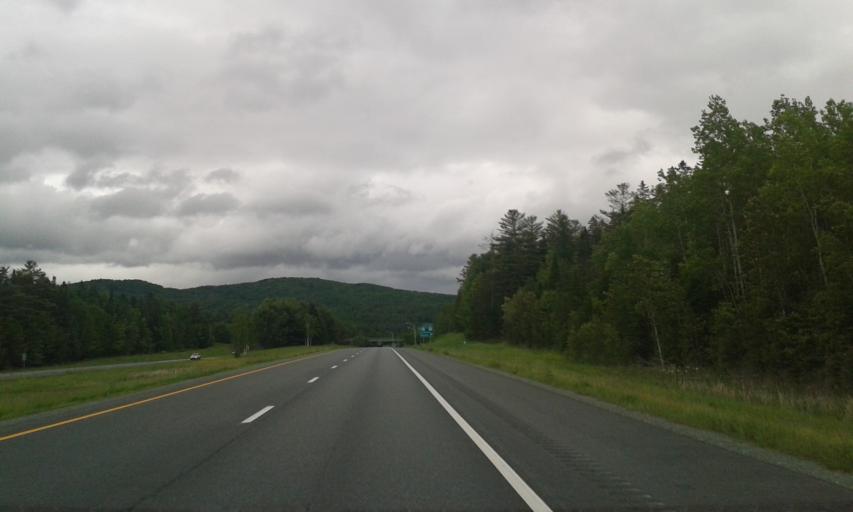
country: US
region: New Hampshire
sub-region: Grafton County
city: Littleton
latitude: 44.3232
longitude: -71.8157
